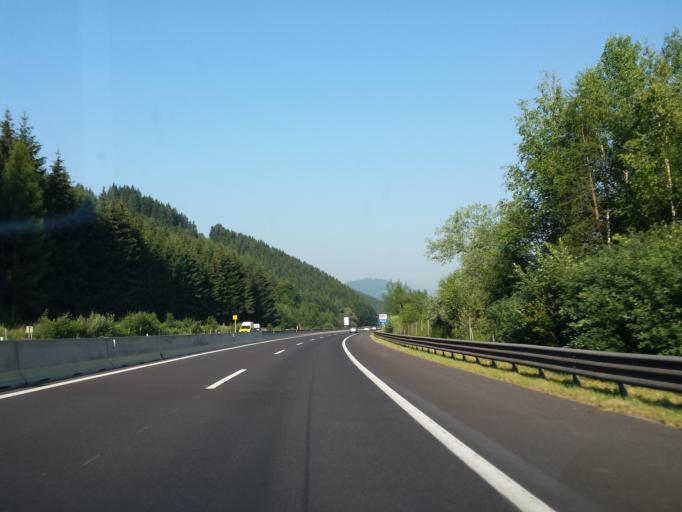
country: AT
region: Styria
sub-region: Politischer Bezirk Bruck-Muerzzuschlag
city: Frauenberg
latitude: 47.4494
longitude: 15.3359
